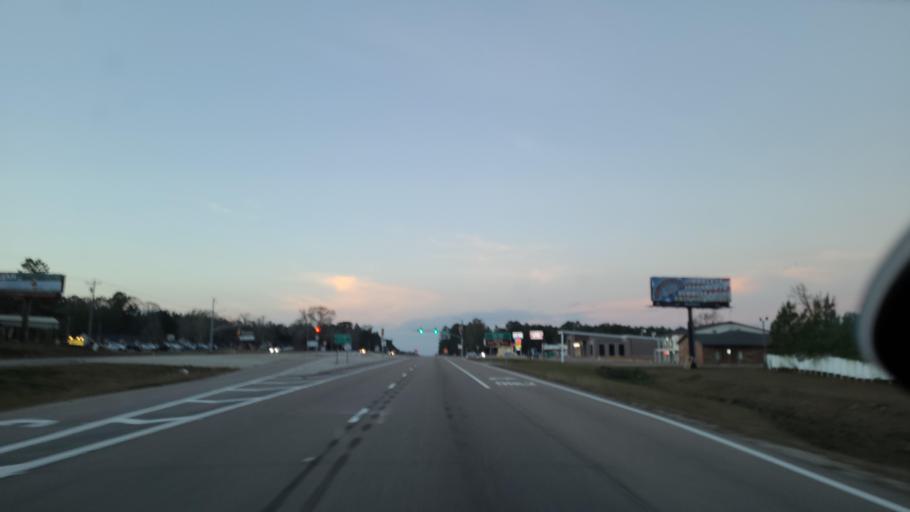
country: US
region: Mississippi
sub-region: Forrest County
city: Hattiesburg
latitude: 31.1851
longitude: -89.2506
